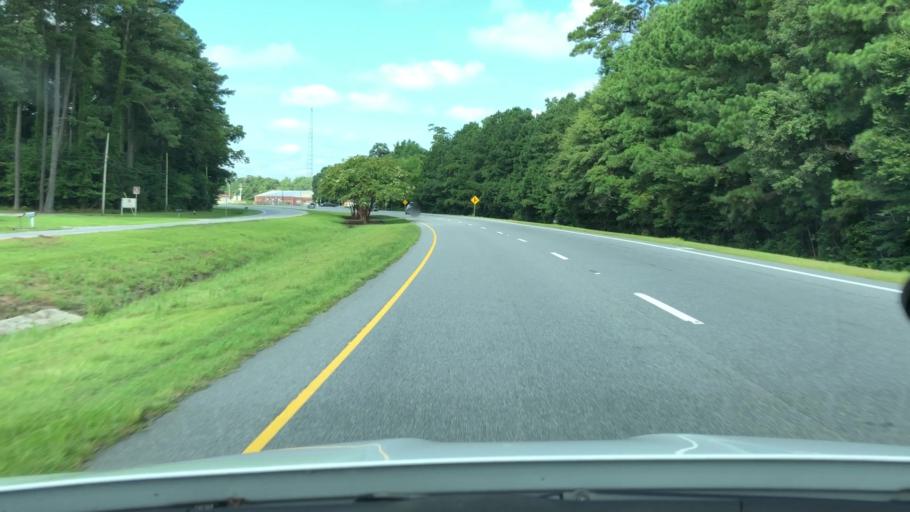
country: US
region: North Carolina
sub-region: Perquimans County
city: Hertford
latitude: 36.2131
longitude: -76.4323
